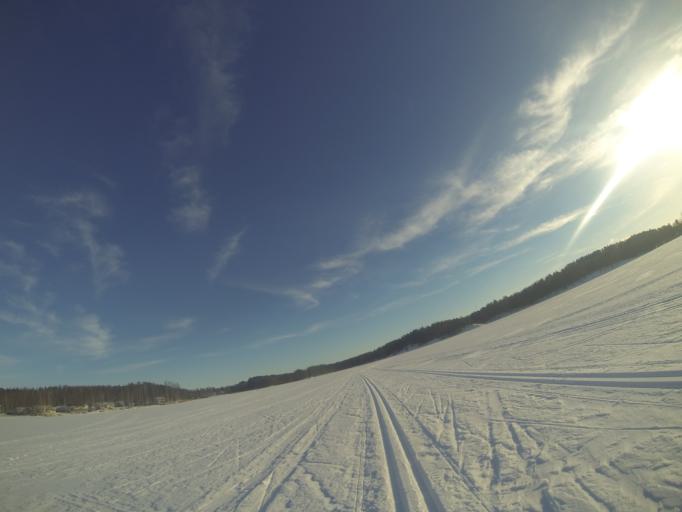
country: FI
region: Southern Savonia
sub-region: Savonlinna
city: Savonlinna
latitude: 61.8824
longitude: 28.9085
